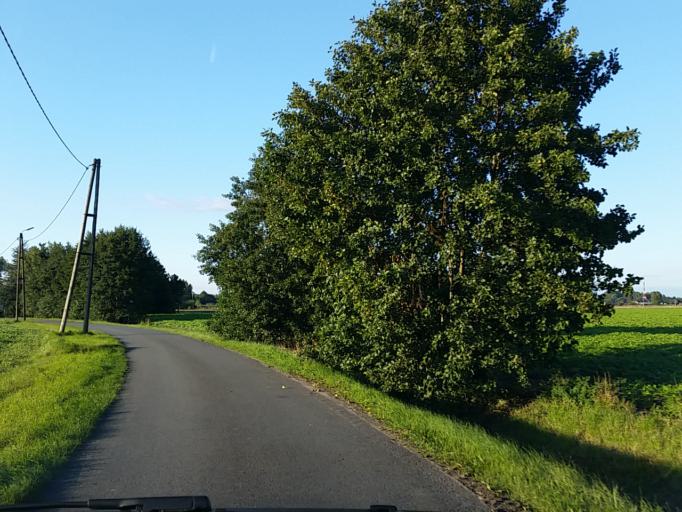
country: BE
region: Flanders
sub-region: Provincie Vlaams-Brabant
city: Steenokkerzeel
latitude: 50.9402
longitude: 4.4856
